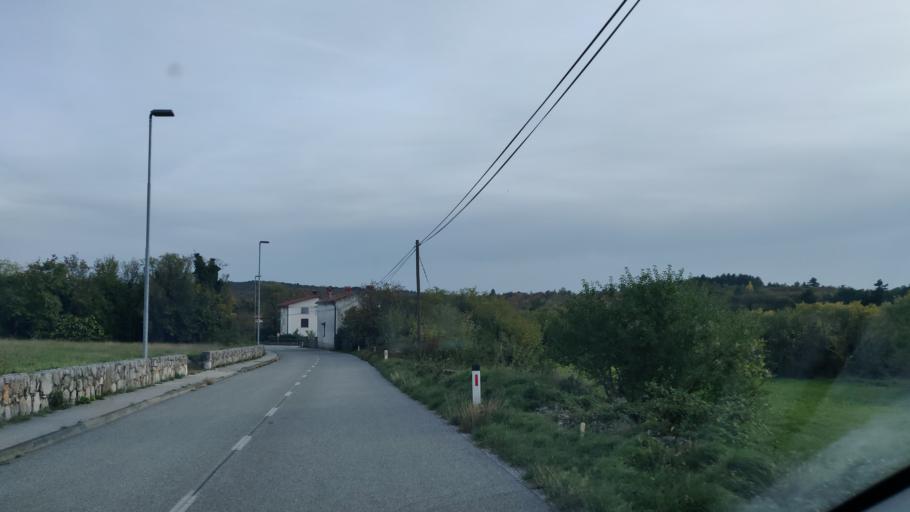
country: SI
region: Miren-Kostanjevica
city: Bilje
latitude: 45.8414
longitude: 13.6438
